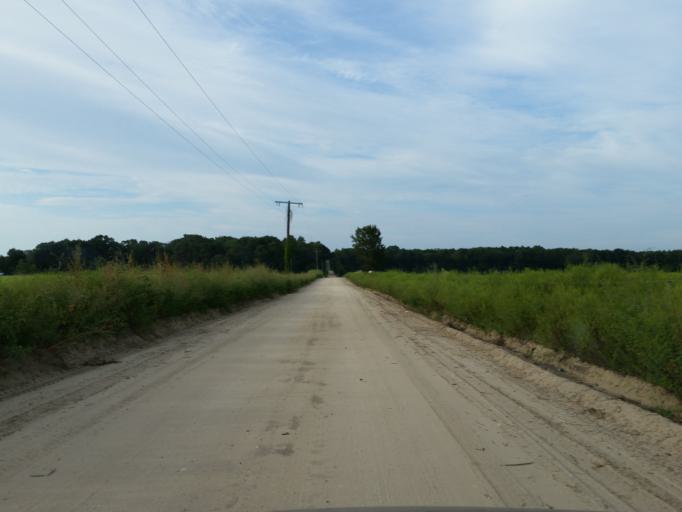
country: US
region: Florida
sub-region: Madison County
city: Madison
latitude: 30.5246
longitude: -83.2158
